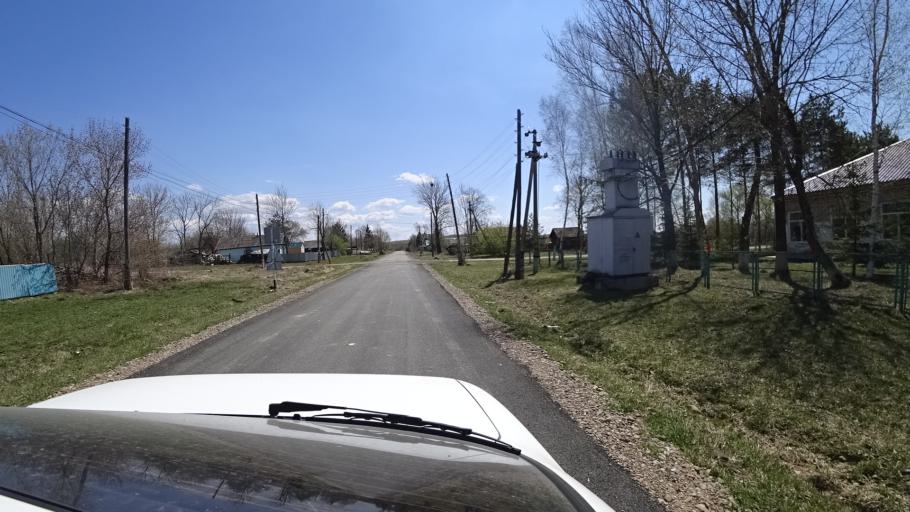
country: RU
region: Primorskiy
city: Dal'nerechensk
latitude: 45.7948
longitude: 133.7685
